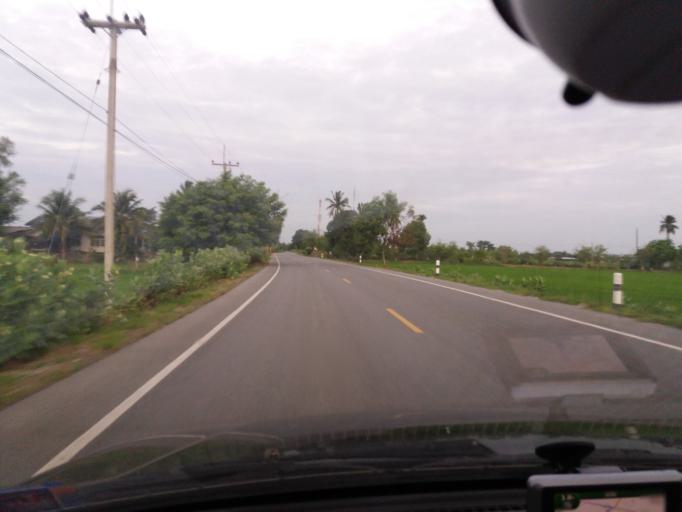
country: TH
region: Suphan Buri
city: Don Chedi
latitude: 14.7069
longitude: 100.0316
